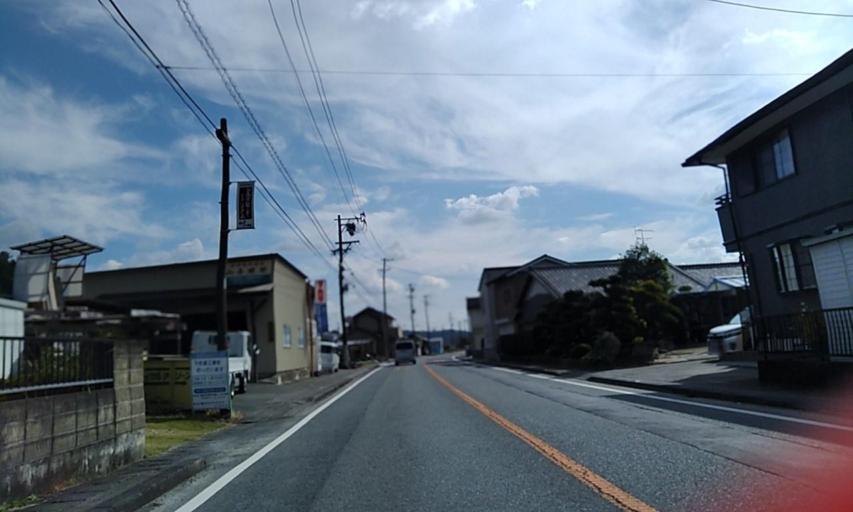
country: JP
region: Shizuoka
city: Hamakita
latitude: 34.8446
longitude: 137.8348
